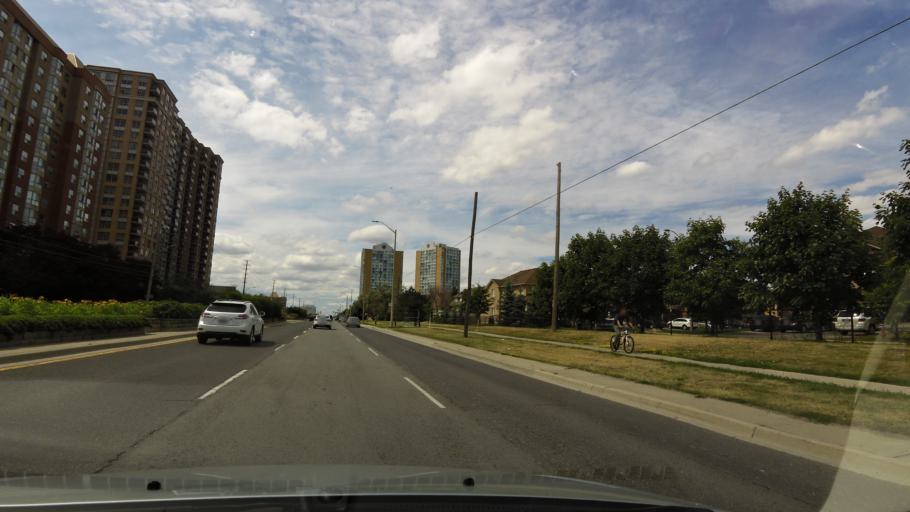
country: CA
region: Ontario
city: Mississauga
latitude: 43.6101
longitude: -79.6575
